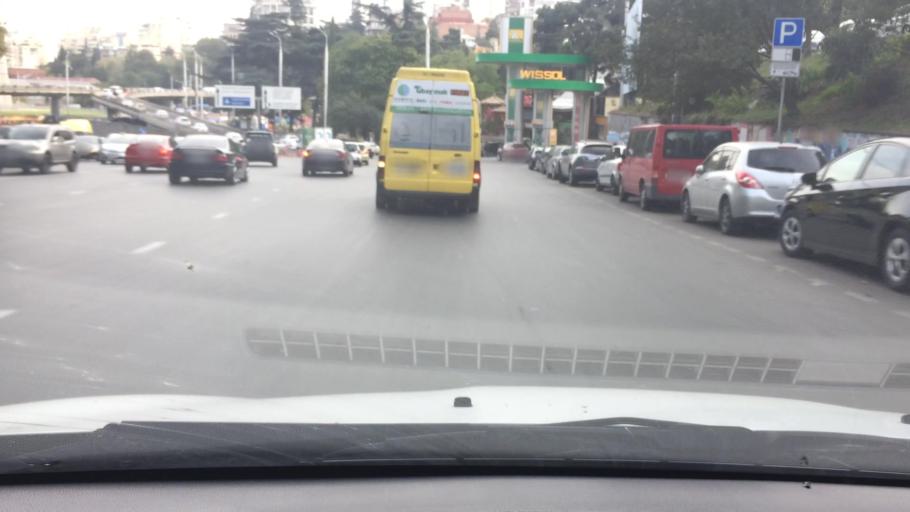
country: GE
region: T'bilisi
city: Tbilisi
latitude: 41.7146
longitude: 44.7795
